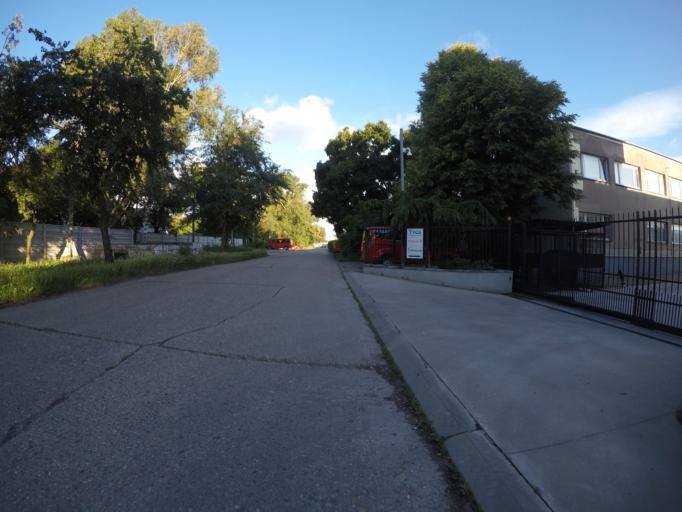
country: SK
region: Bratislavsky
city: Bratislava
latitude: 48.1724
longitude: 17.1533
